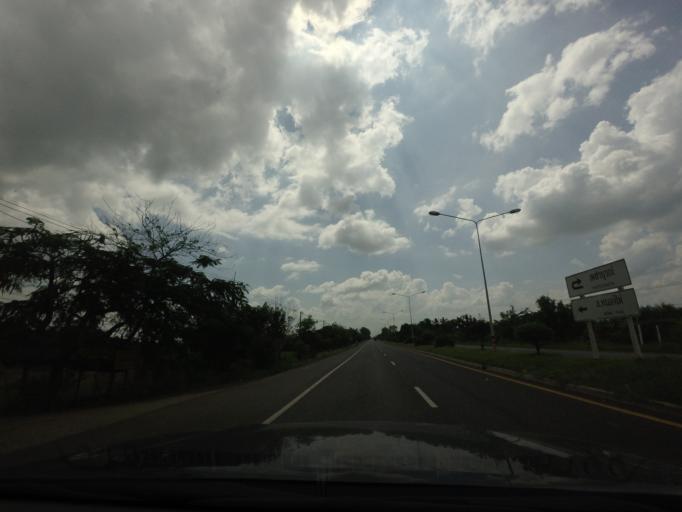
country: TH
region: Phetchabun
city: Nong Phai
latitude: 16.1827
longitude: 101.0875
